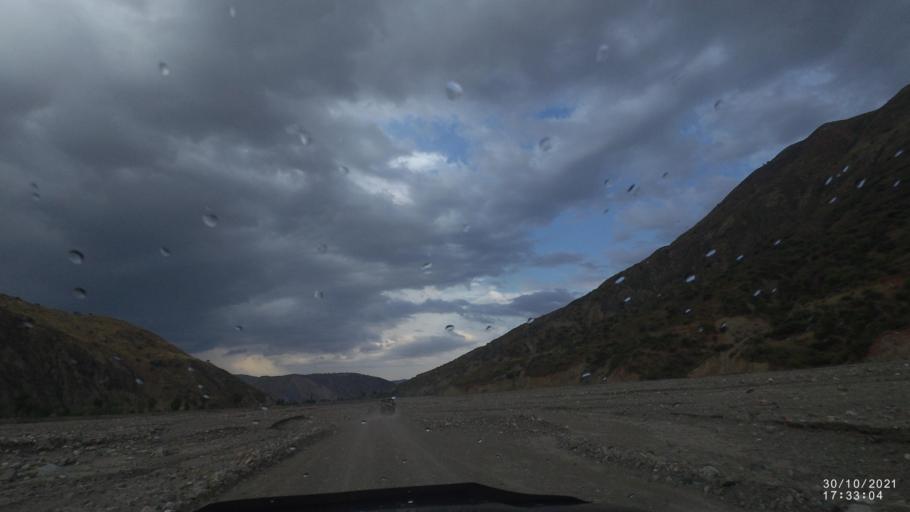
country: BO
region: Cochabamba
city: Sipe Sipe
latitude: -17.5265
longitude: -66.5838
